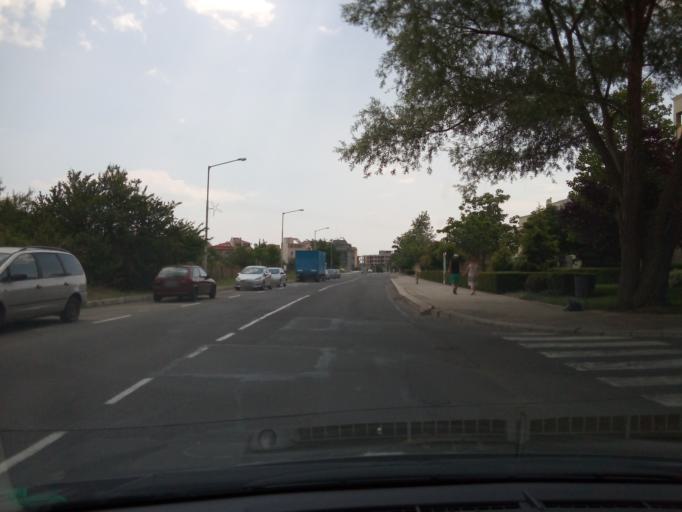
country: BG
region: Burgas
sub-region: Obshtina Nesebur
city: Ravda
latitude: 42.6540
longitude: 27.6997
